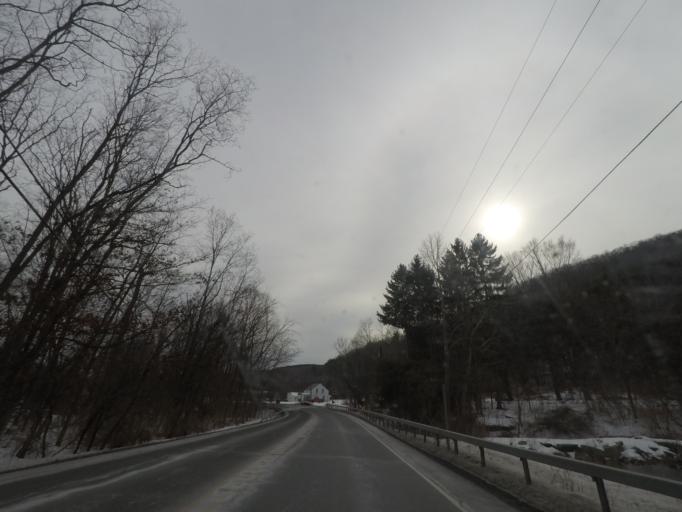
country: US
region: New York
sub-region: Albany County
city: Voorheesville
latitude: 42.5873
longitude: -73.9834
